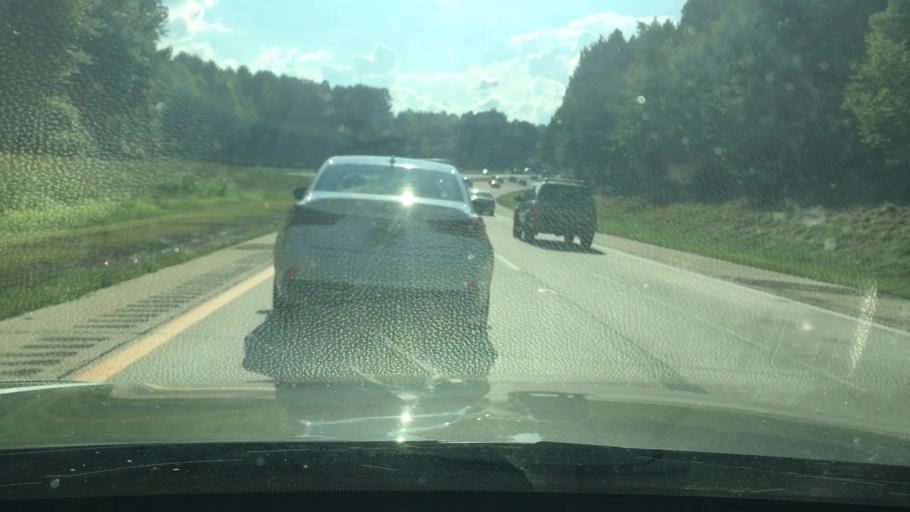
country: US
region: North Carolina
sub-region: Orange County
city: Hillsborough
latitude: 36.0612
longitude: -79.1316
